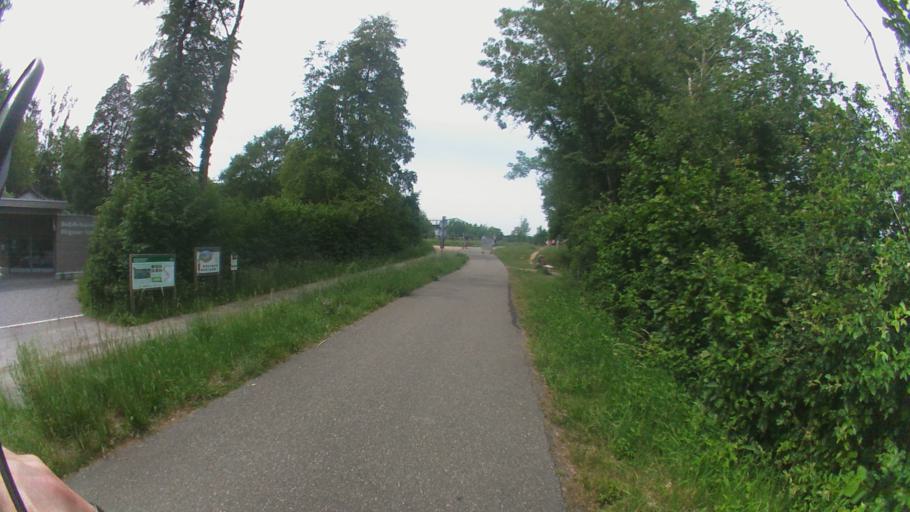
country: CH
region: Aargau
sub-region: Bezirk Zurzach
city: Klingnau
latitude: 47.5769
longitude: 8.2395
